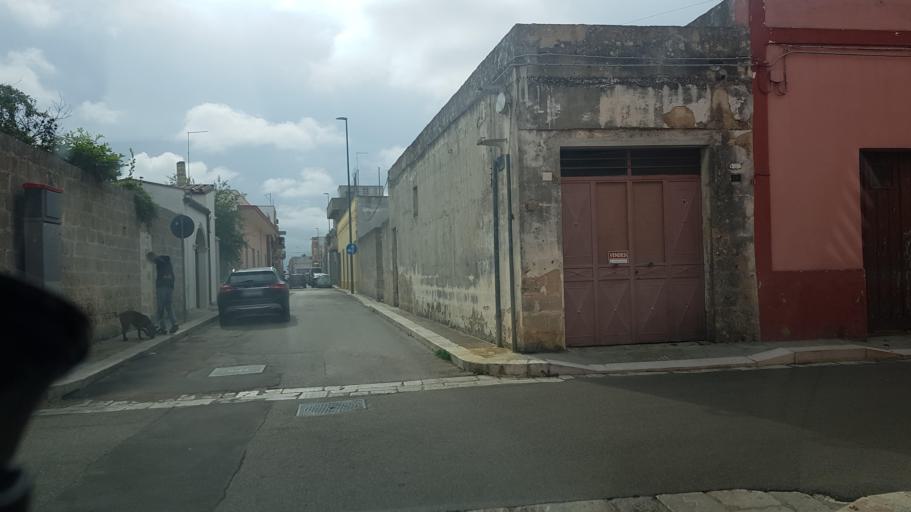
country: IT
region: Apulia
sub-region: Provincia di Lecce
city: Guagnano
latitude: 40.4026
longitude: 17.9480
